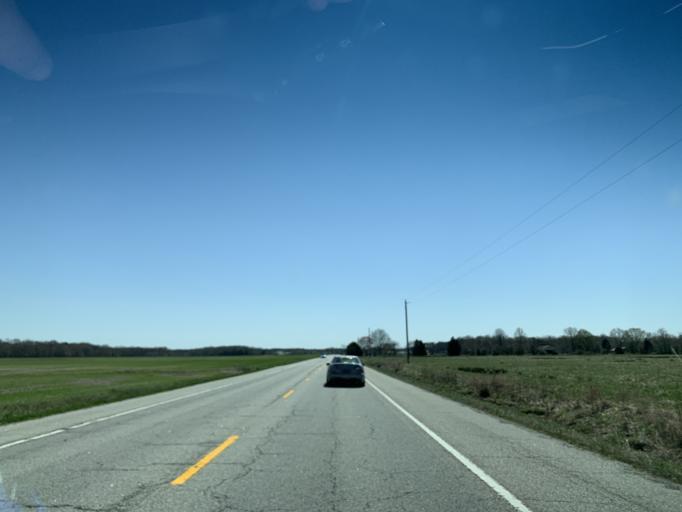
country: US
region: Maryland
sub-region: Queen Anne's County
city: Centreville
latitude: 38.9885
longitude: -76.0263
